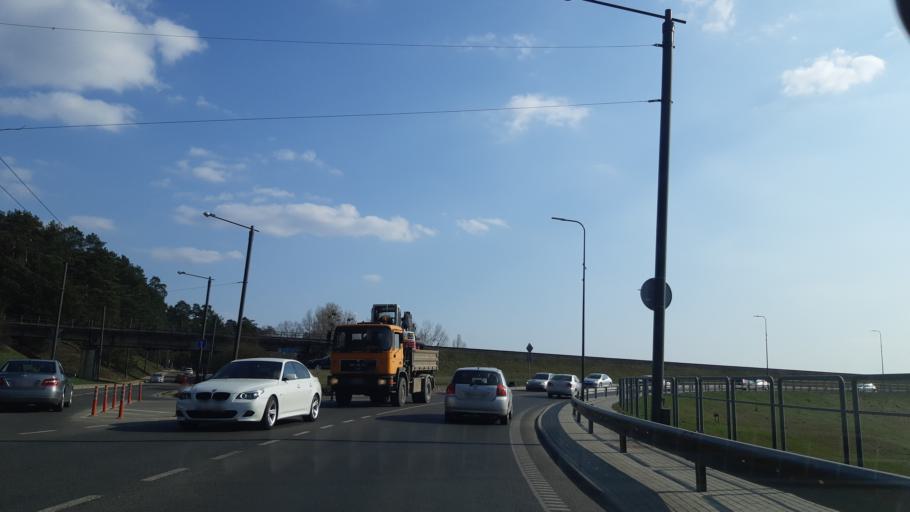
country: LT
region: Kauno apskritis
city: Dainava (Kaunas)
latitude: 54.8801
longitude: 24.0113
